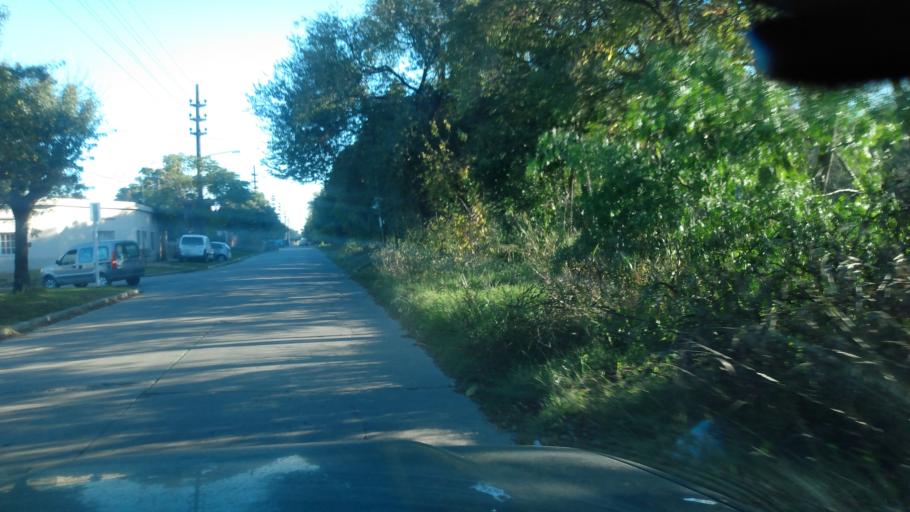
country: AR
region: Buenos Aires
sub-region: Partido de Lujan
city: Lujan
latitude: -34.5600
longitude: -59.1011
